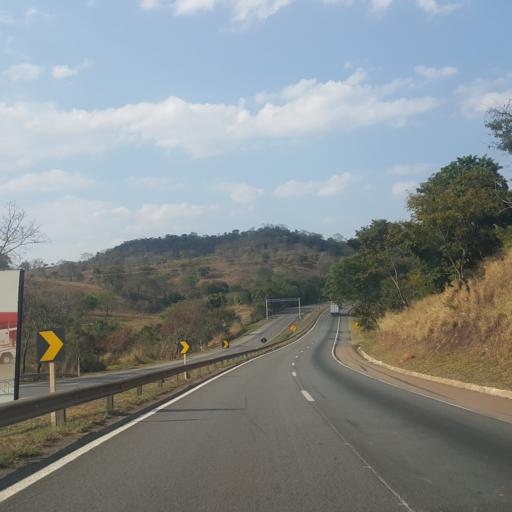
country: BR
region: Goias
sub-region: Abadiania
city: Abadiania
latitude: -16.1128
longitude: -48.5875
